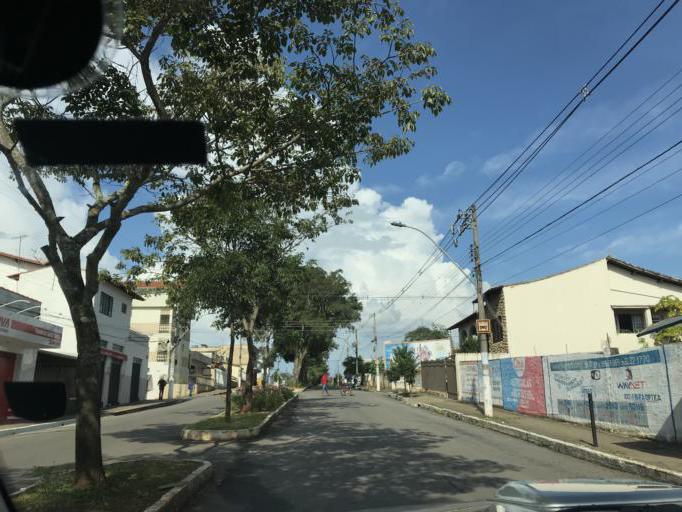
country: BR
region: Minas Gerais
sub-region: Tres Coracoes
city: Tres Coracoes
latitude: -21.7033
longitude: -45.2518
